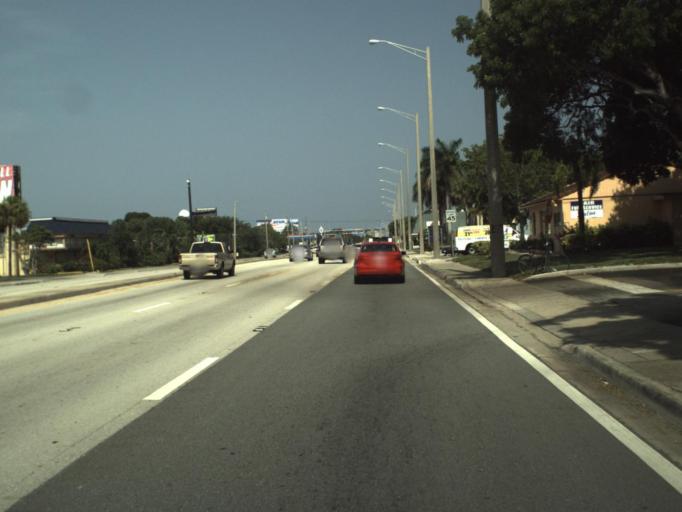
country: US
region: Florida
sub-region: Broward County
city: Tedder
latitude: 26.2750
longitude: -80.1182
